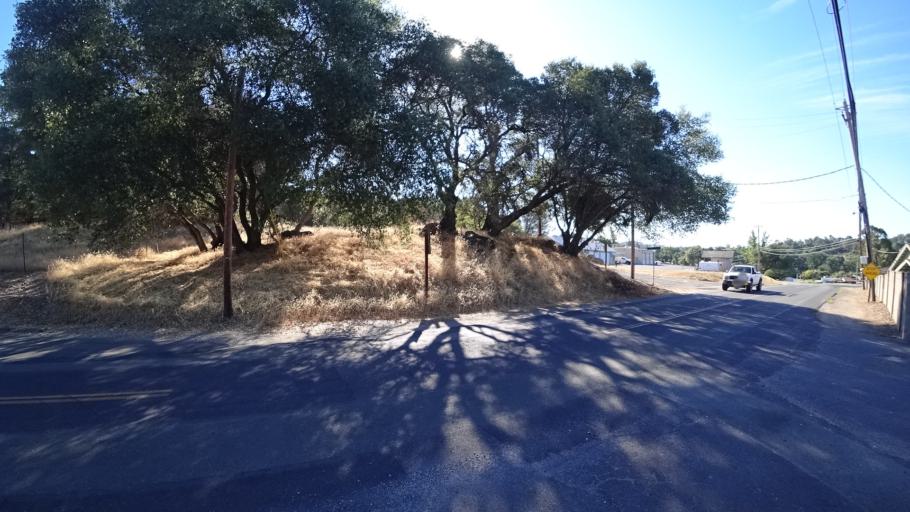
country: US
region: California
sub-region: Calaveras County
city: San Andreas
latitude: 38.1924
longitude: -120.6709
